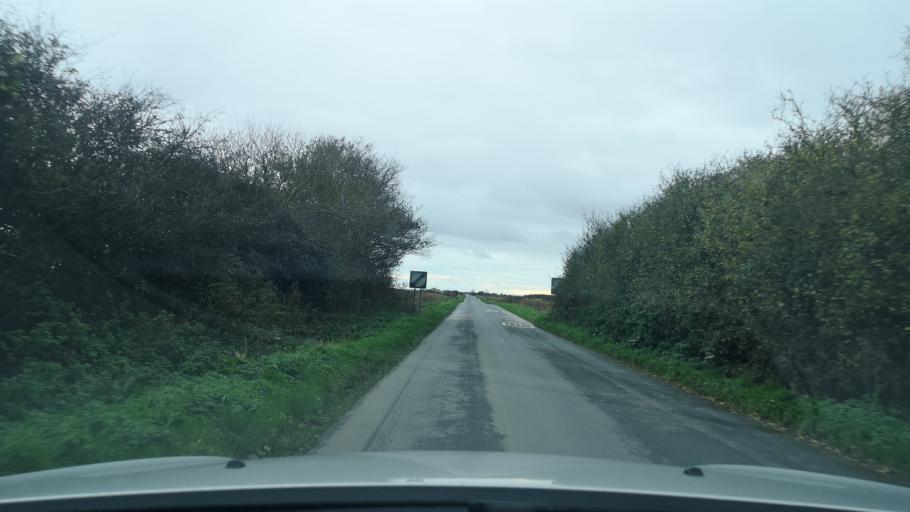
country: GB
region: England
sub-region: East Riding of Yorkshire
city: Easington
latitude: 53.6478
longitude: 0.1235
